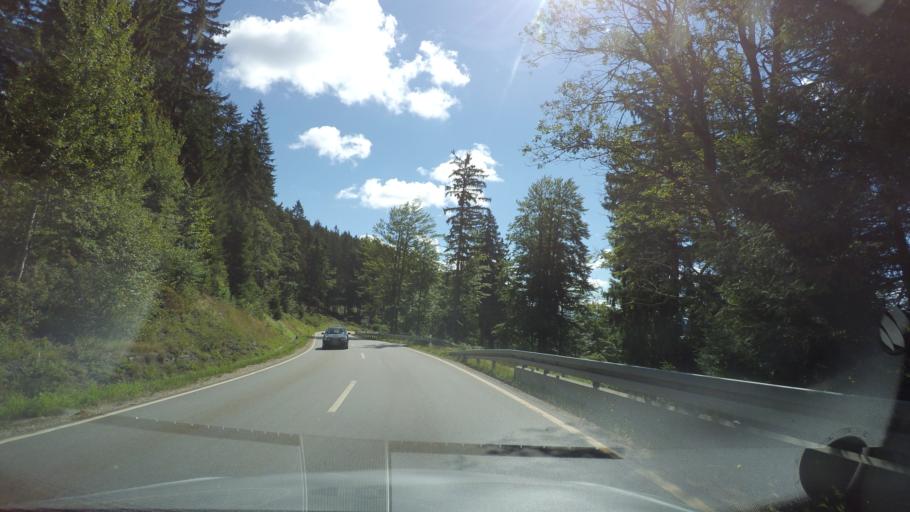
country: DE
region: Bavaria
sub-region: Lower Bavaria
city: Bodenmais
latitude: 49.0693
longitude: 13.1301
